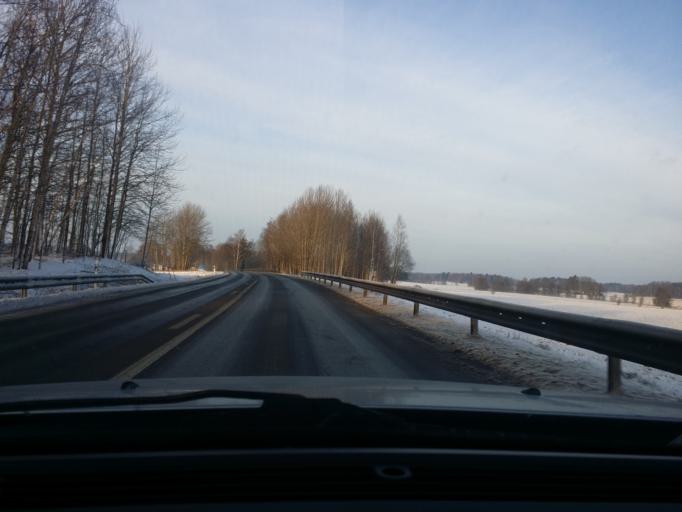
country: SE
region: OErebro
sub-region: Lindesbergs Kommun
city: Fellingsbro
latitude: 59.4661
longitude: 15.5549
